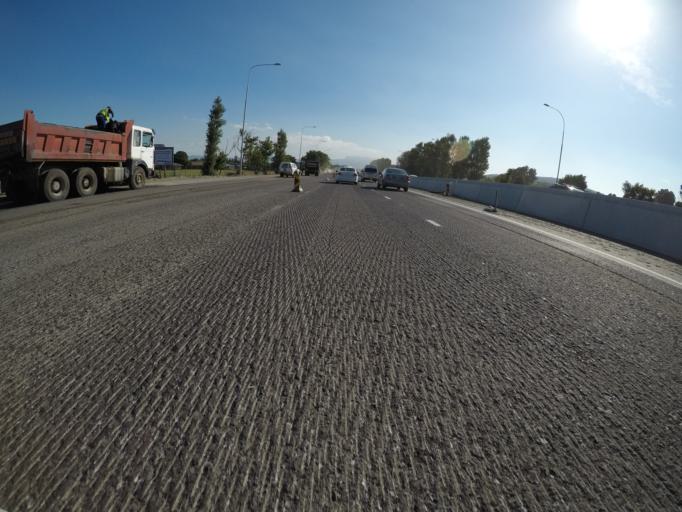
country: ZA
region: Western Cape
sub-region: City of Cape Town
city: Kraaifontein
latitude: -33.8839
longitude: 18.6426
